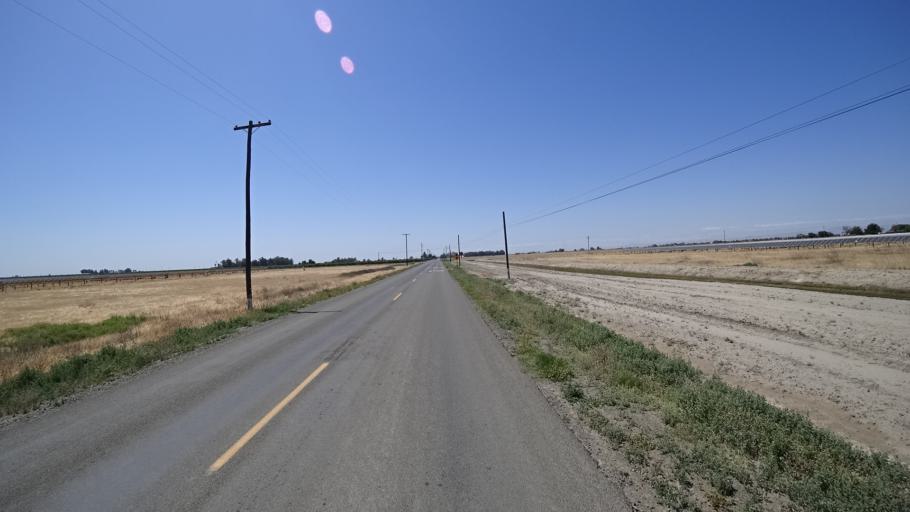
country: US
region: California
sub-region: Kings County
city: Stratford
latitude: 36.2134
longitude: -119.7982
